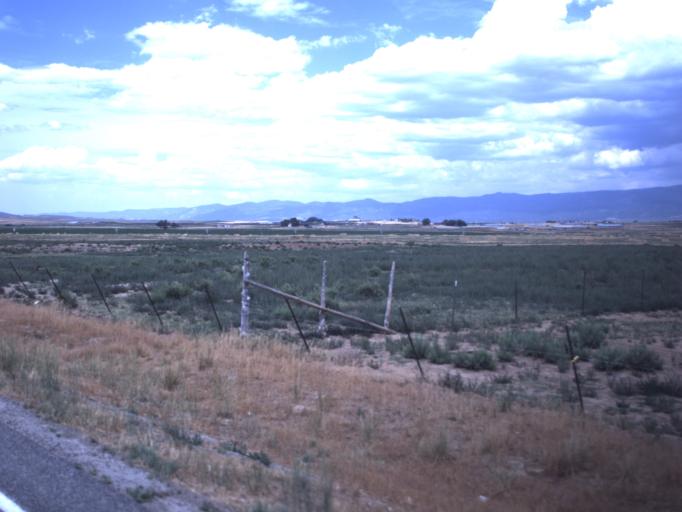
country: US
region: Utah
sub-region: Sanpete County
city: Moroni
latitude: 39.4630
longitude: -111.5627
